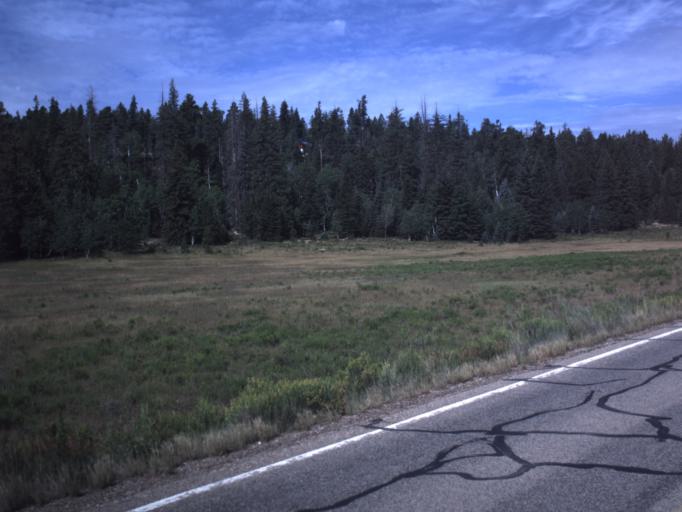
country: US
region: Utah
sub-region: Iron County
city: Parowan
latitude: 37.5219
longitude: -112.6549
